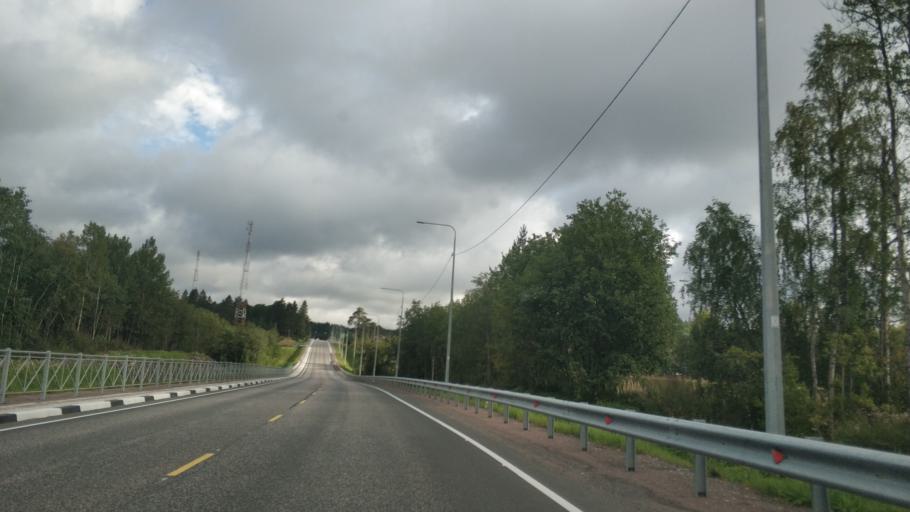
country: RU
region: Republic of Karelia
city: Khelyulya
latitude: 61.8168
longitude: 30.6315
